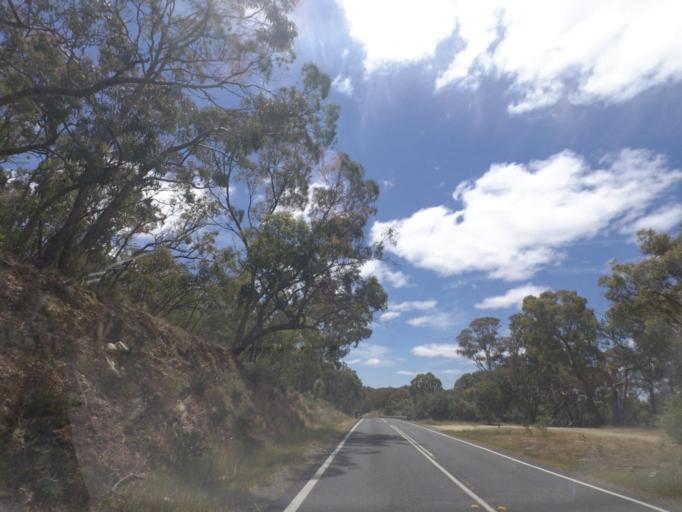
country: AU
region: Victoria
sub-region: Mount Alexander
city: Castlemaine
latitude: -37.2918
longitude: 144.1631
